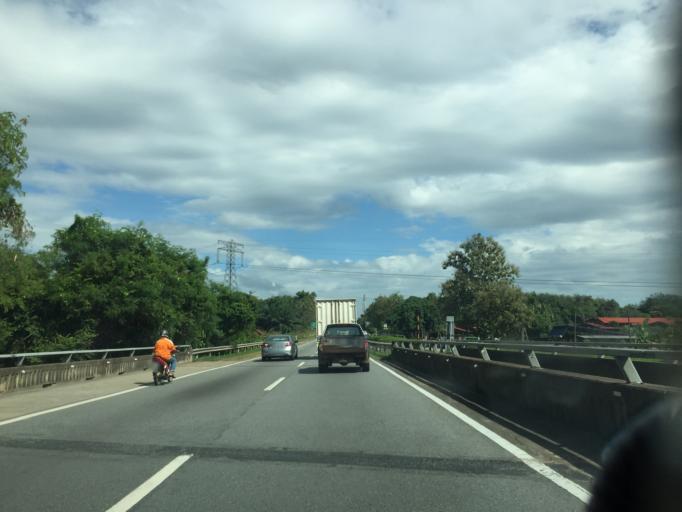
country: MY
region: Kedah
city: Jitra
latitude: 6.3230
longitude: 100.4203
